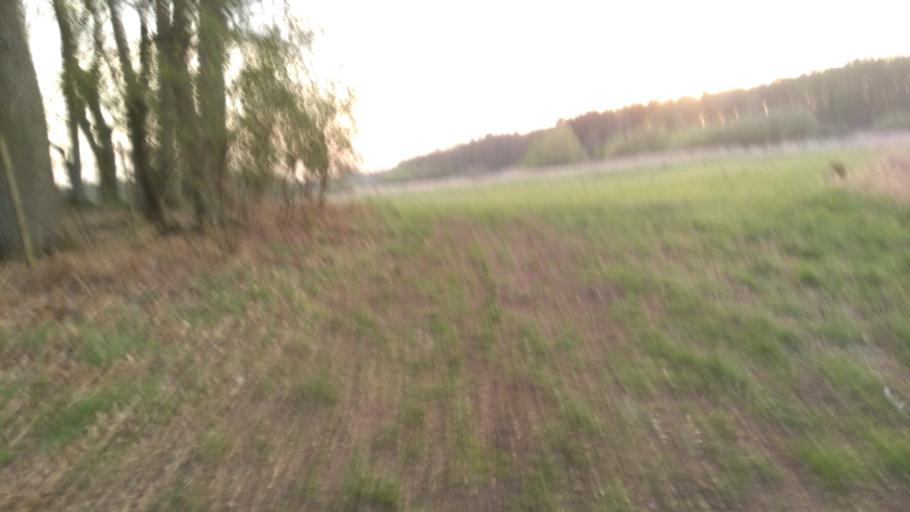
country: DE
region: Lower Saxony
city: Bliedersdorf
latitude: 53.4800
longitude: 9.5411
